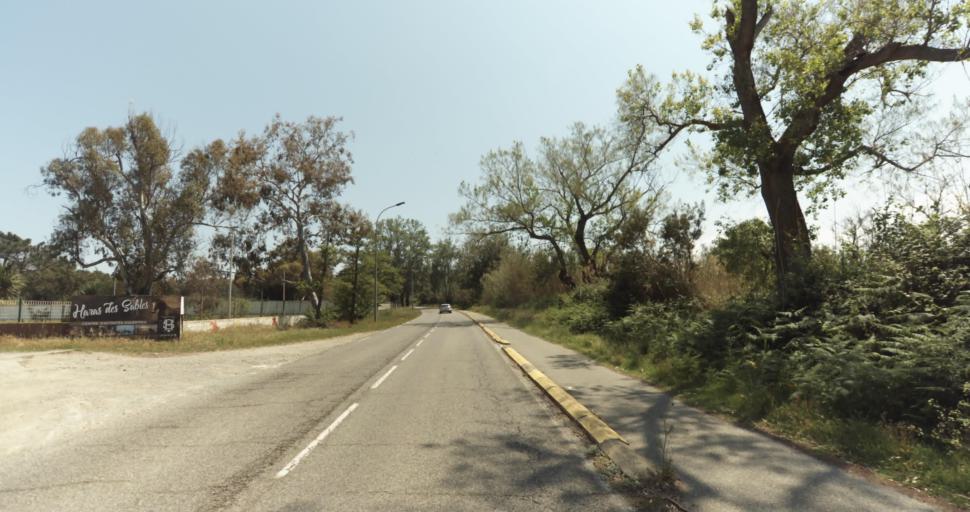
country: FR
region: Corsica
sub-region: Departement de la Haute-Corse
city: Biguglia
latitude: 42.6262
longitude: 9.4690
